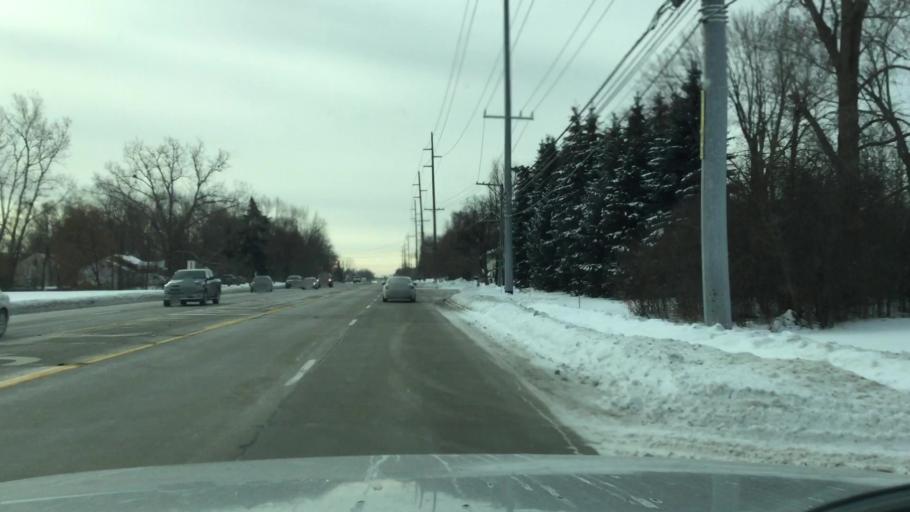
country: US
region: Michigan
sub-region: Oakland County
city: Troy
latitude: 42.5990
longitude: -83.1295
